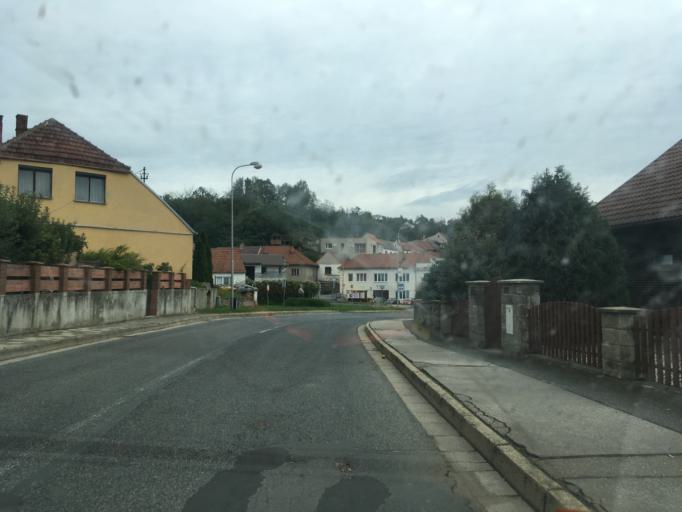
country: CZ
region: South Moravian
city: Oslavany
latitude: 49.1277
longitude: 16.3260
